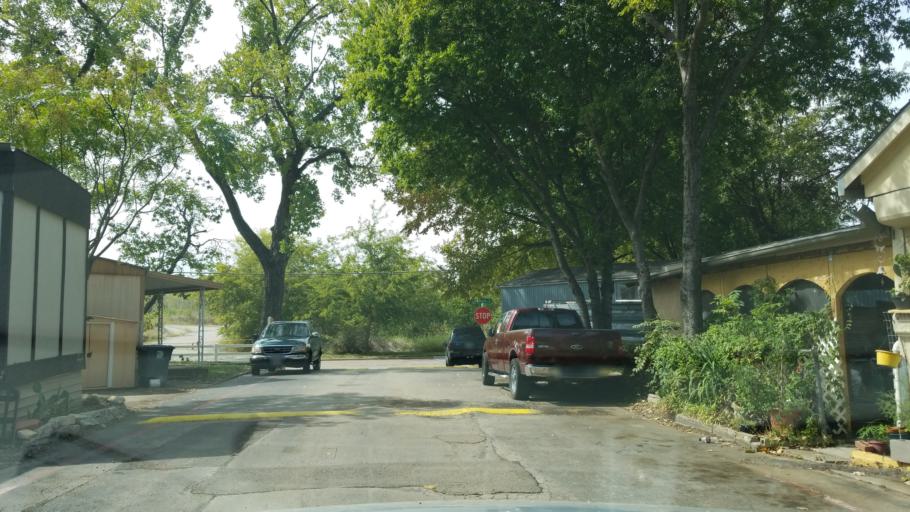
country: US
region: Texas
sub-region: Dallas County
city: Highland Park
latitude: 32.7878
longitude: -96.7236
